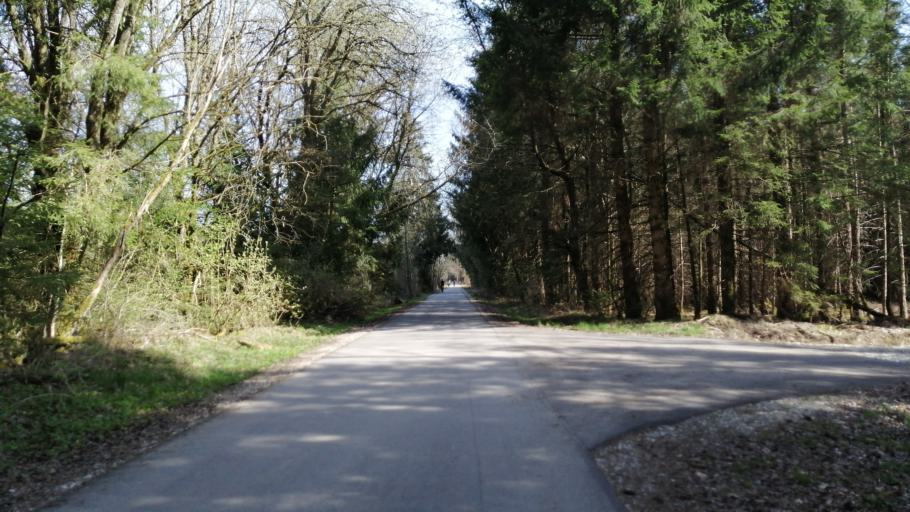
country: DE
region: Bavaria
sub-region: Upper Bavaria
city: Sauerlach
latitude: 47.9889
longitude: 11.6282
